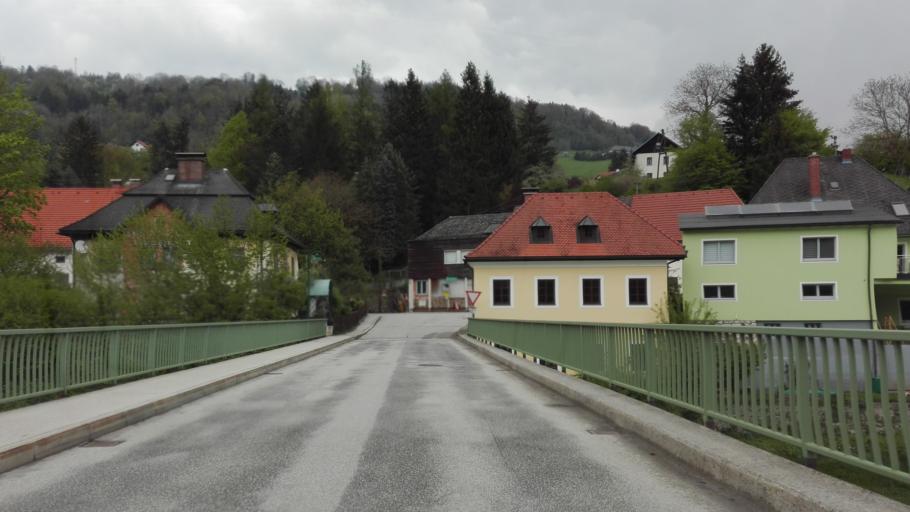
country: AT
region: Upper Austria
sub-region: Politischer Bezirk Steyr-Land
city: Losenstein
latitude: 47.9244
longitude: 14.4334
